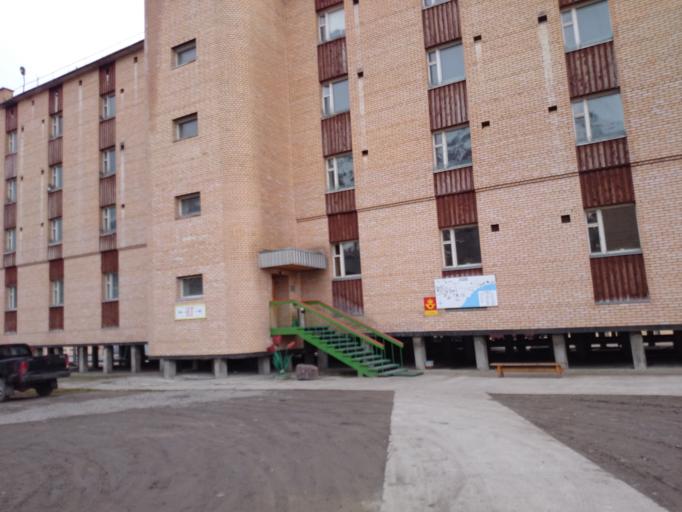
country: SJ
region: Svalbard
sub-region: Spitsbergen
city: Longyearbyen
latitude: 78.6552
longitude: 16.3264
